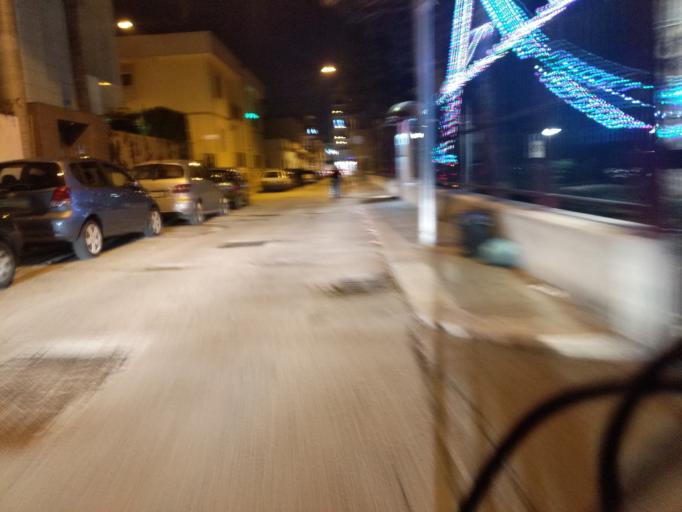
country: IT
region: Apulia
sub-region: Provincia di Bari
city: Modugno
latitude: 41.0854
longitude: 16.7884
